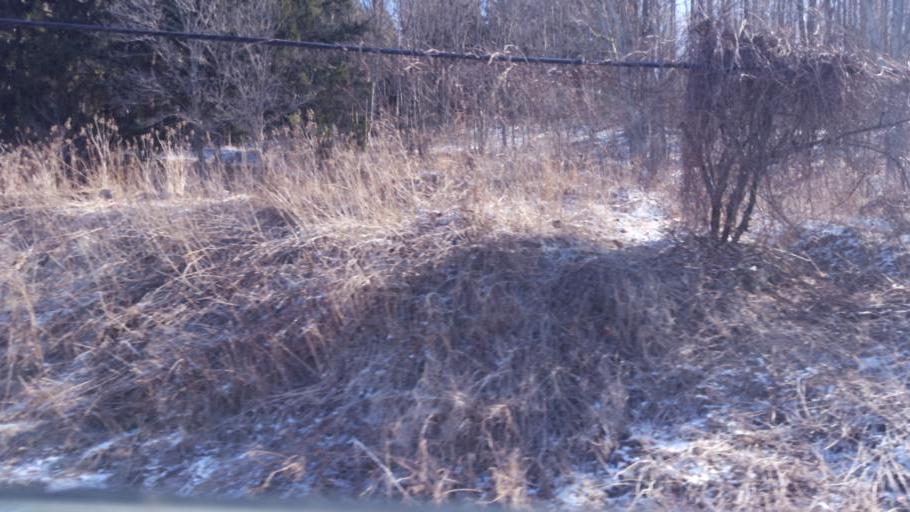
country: US
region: New York
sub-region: Allegany County
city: Wellsville
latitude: 42.1299
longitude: -77.9497
